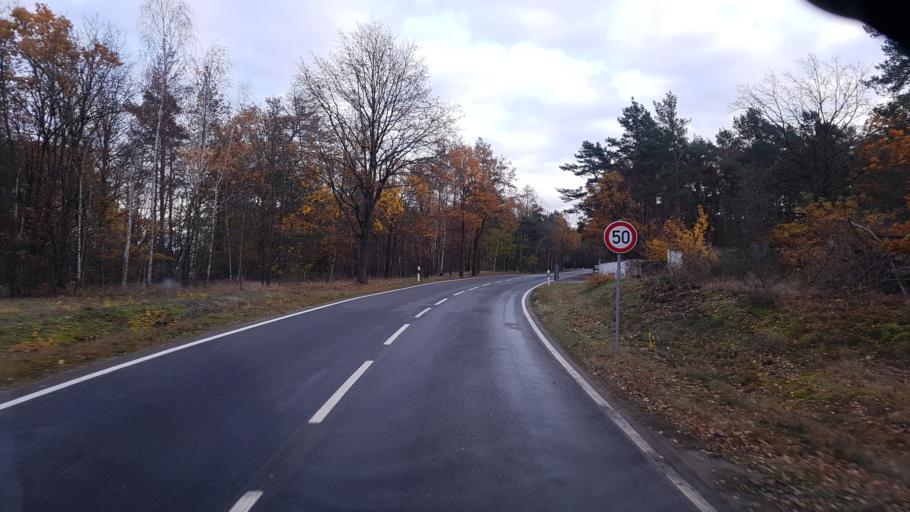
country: DE
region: Brandenburg
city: Ortrand
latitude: 51.3828
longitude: 13.7735
